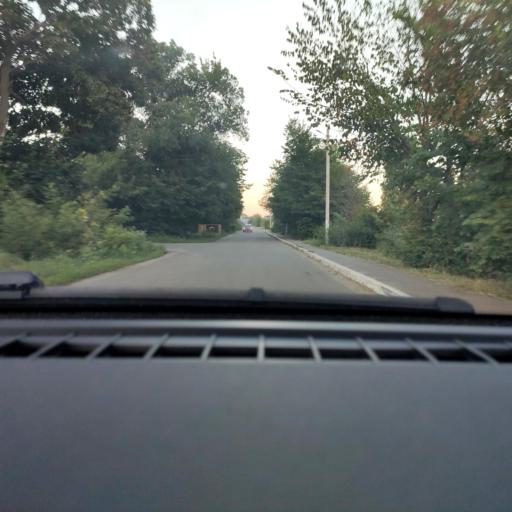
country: RU
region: Voronezj
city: Novaya Usman'
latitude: 51.6565
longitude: 39.3309
